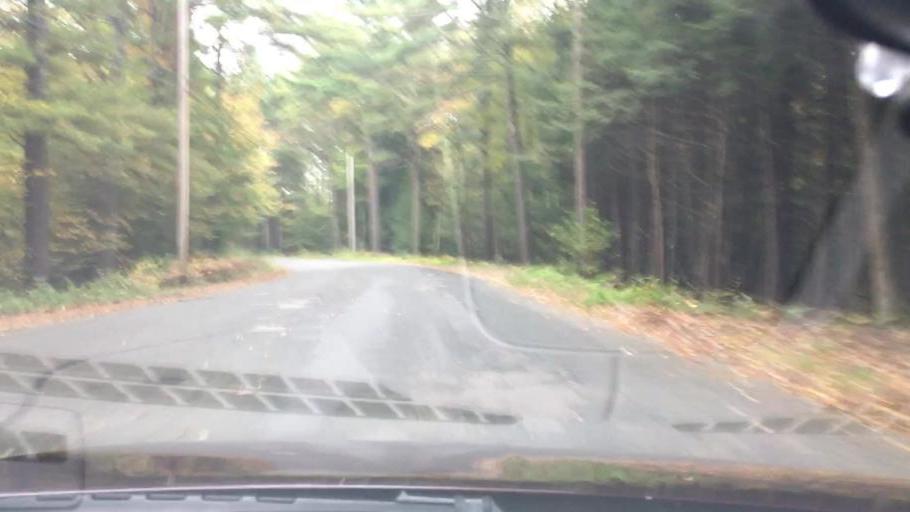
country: US
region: Connecticut
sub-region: Tolland County
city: Stafford
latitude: 41.9949
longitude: -72.3276
